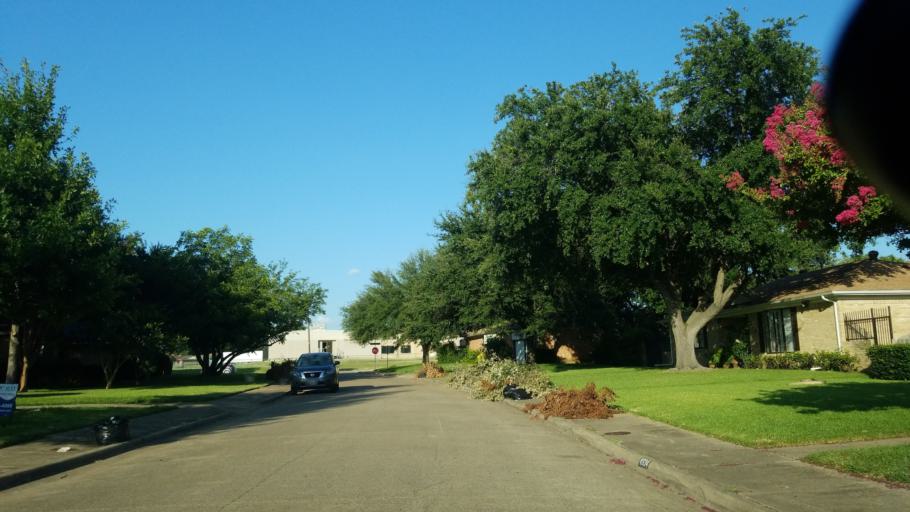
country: US
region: Texas
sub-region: Dallas County
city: Highland Park
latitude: 32.7848
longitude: -96.7086
